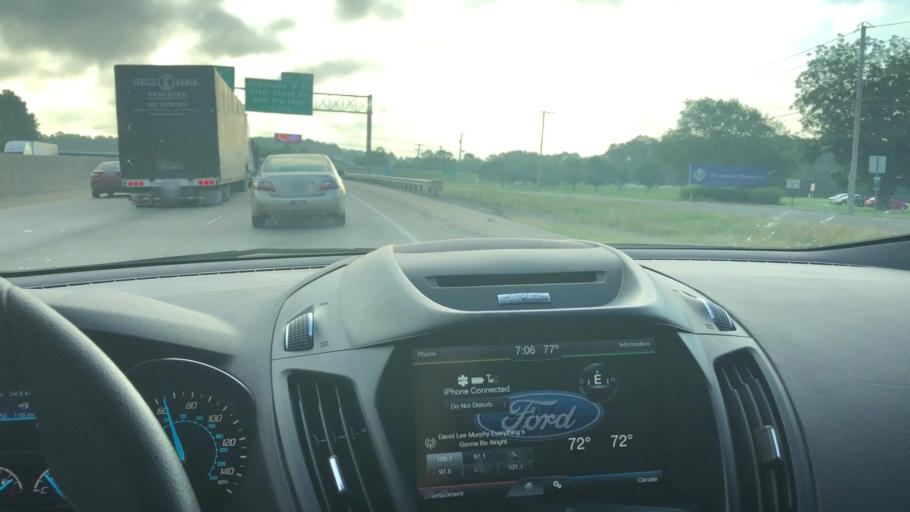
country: US
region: Arkansas
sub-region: Pulaski County
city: Alexander
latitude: 34.6477
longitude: -92.4212
